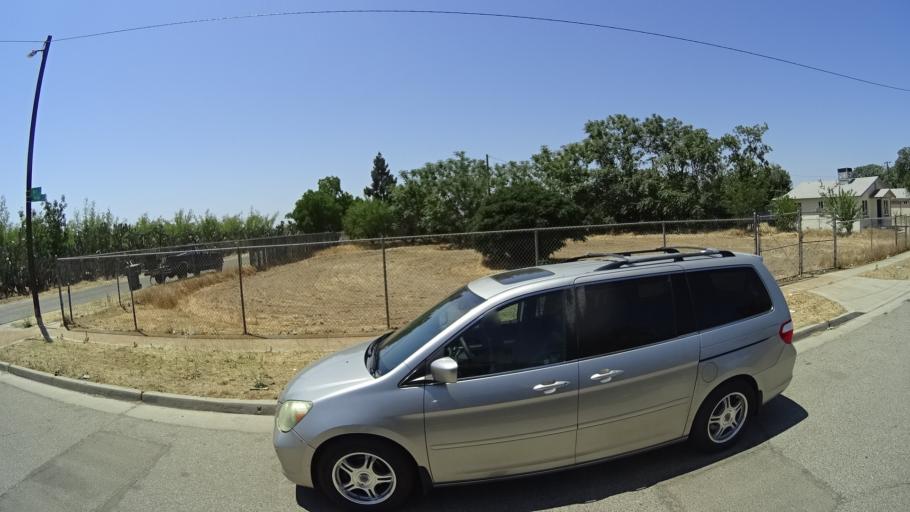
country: US
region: California
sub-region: Fresno County
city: West Park
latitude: 36.7095
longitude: -119.8068
